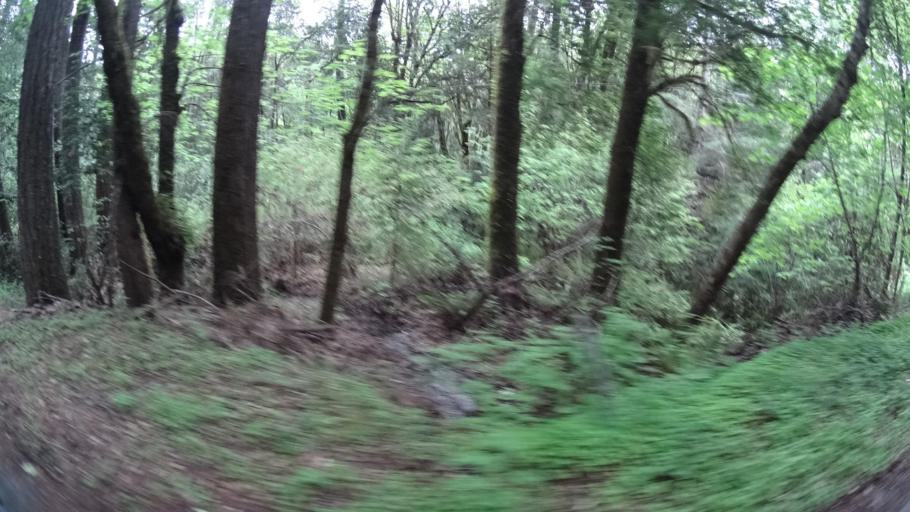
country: US
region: California
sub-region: Humboldt County
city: Blue Lake
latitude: 40.9584
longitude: -123.8378
